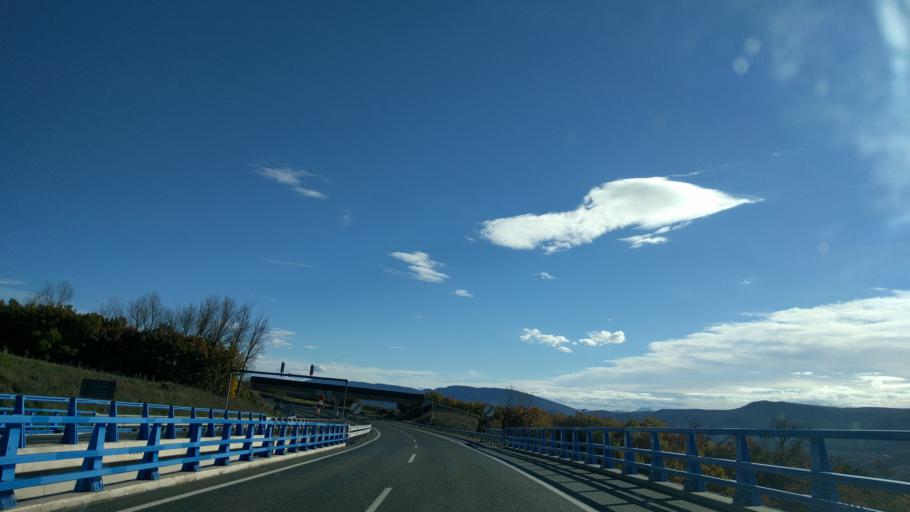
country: ES
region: Navarre
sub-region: Provincia de Navarra
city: Yesa
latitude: 42.6225
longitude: -1.1661
